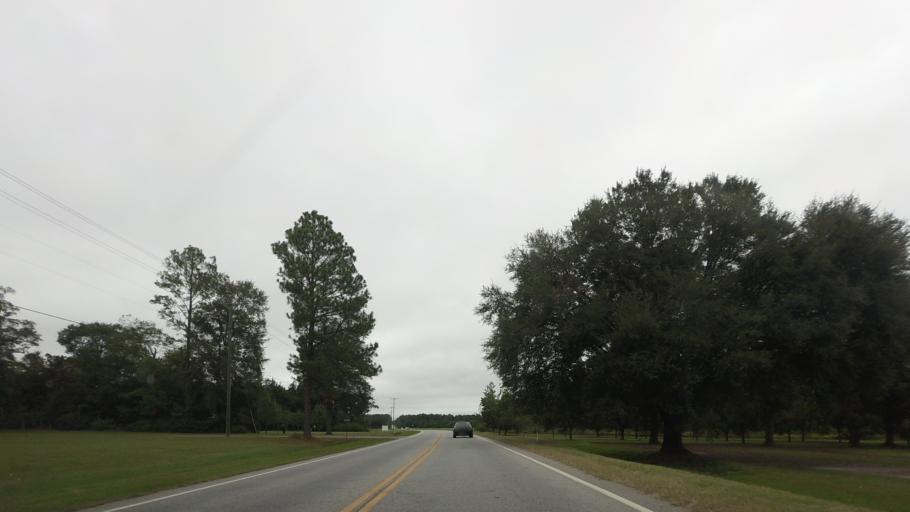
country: US
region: Georgia
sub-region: Berrien County
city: Ray City
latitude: 31.0051
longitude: -83.1985
